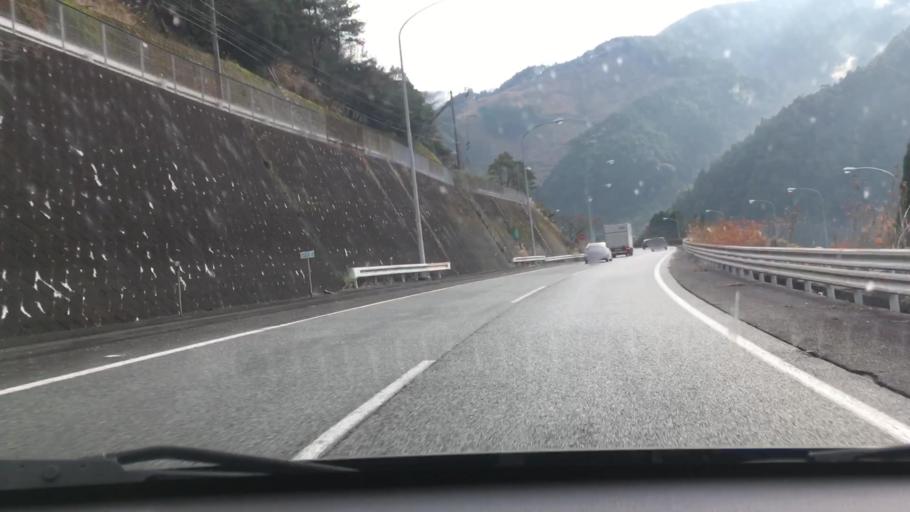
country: JP
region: Kumamoto
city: Yatsushiro
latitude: 32.4052
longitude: 130.6978
